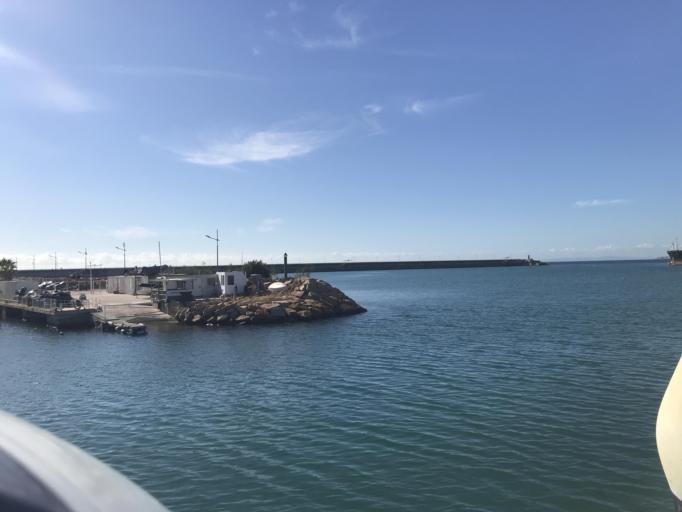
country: ES
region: Valencia
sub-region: Provincia de Alicante
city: Torrevieja
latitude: 37.9714
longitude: -0.6852
